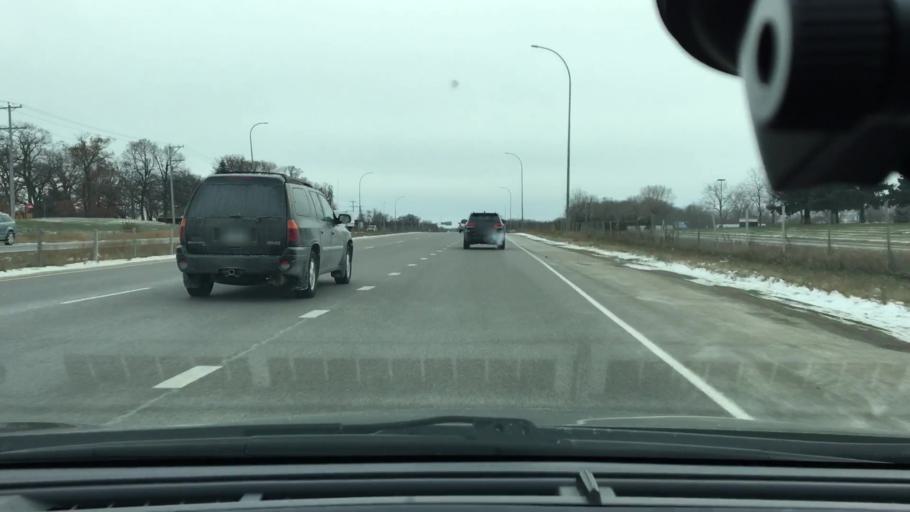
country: US
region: Minnesota
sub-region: Hennepin County
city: Osseo
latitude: 45.0903
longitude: -93.4026
